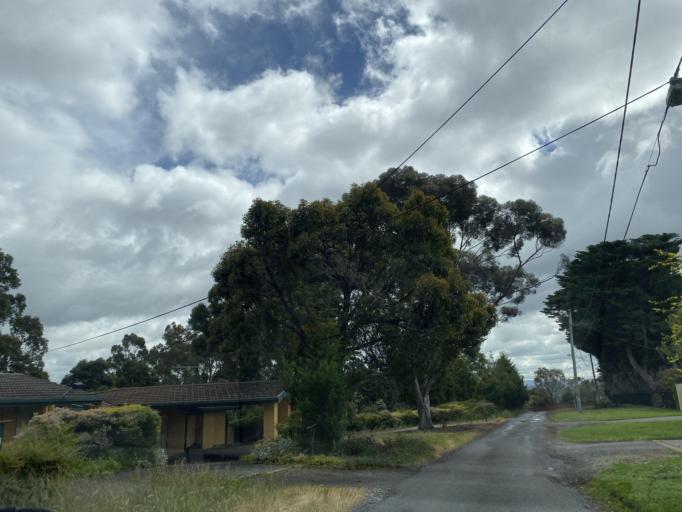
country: AU
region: Victoria
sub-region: Manningham
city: Templestowe Lower
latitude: -37.7615
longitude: 145.1397
